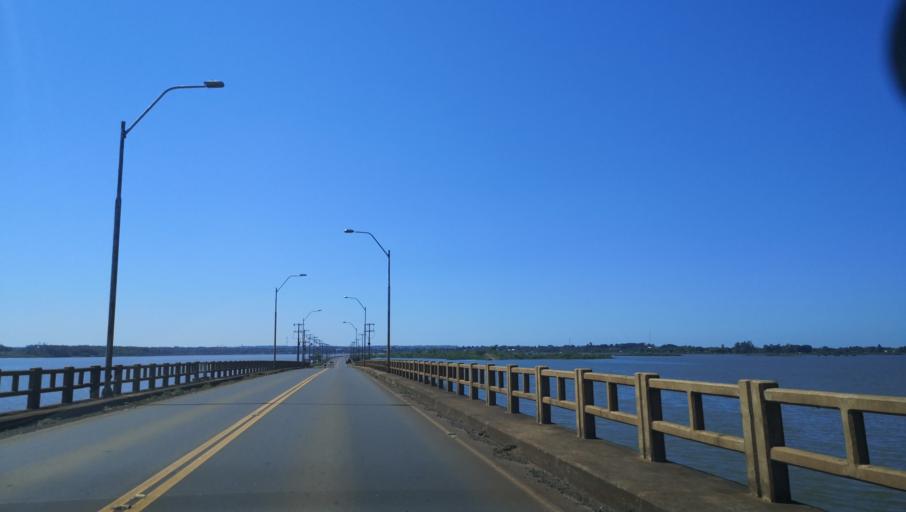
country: PY
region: Itapua
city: Carmen del Parana
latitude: -27.2052
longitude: -56.1692
